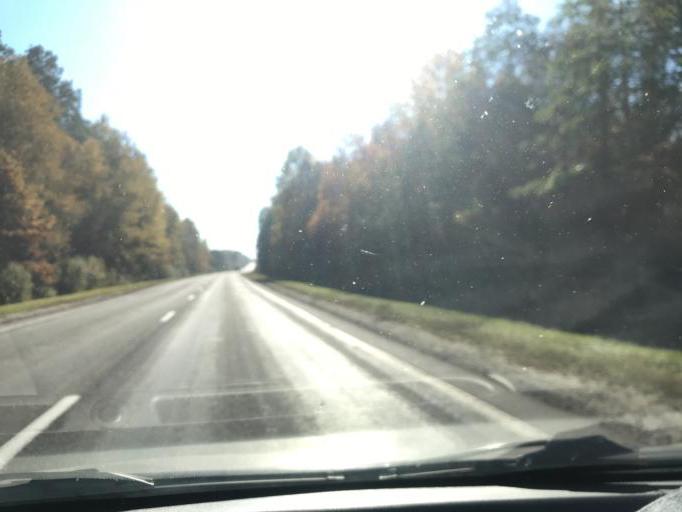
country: BY
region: Gomel
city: Kastsyukowka
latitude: 52.4269
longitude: 30.8280
